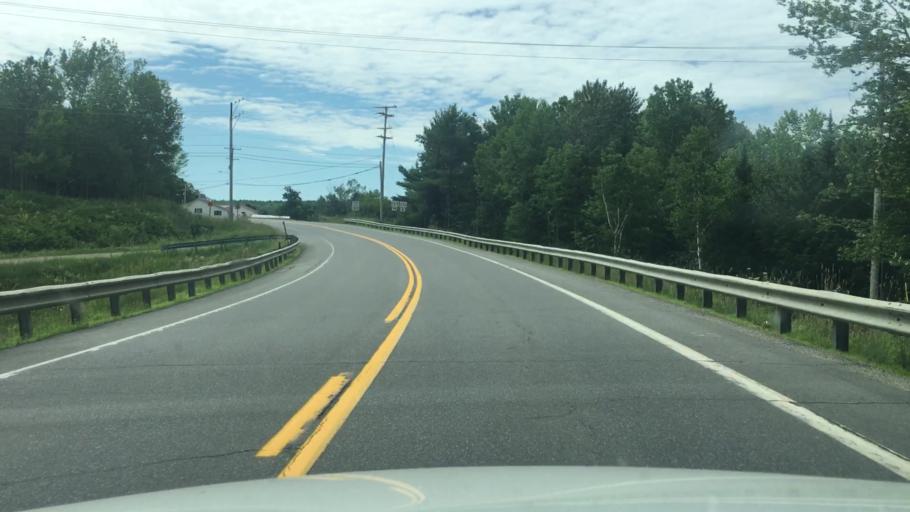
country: US
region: Maine
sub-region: Waldo County
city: Troy
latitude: 44.5816
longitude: -69.2792
